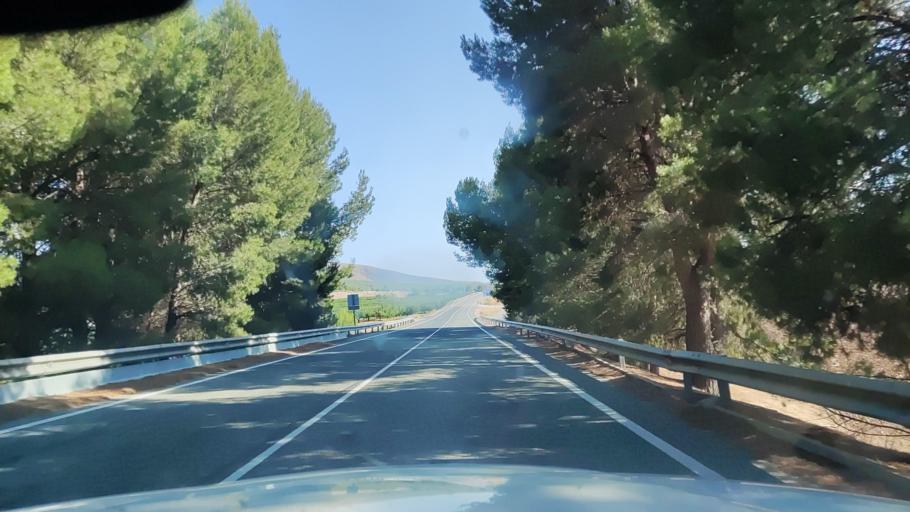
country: ES
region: Castille-La Mancha
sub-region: Provincia de Albacete
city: Tobarra
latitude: 38.6384
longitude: -1.6675
